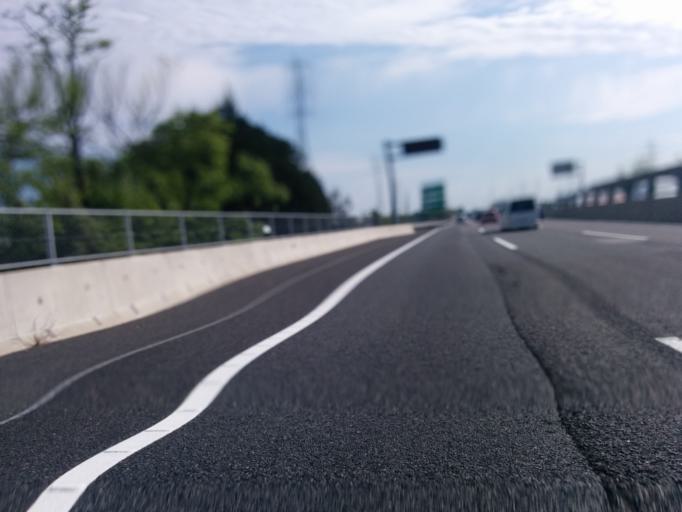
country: JP
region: Mie
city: Komono
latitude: 34.9984
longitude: 136.5580
